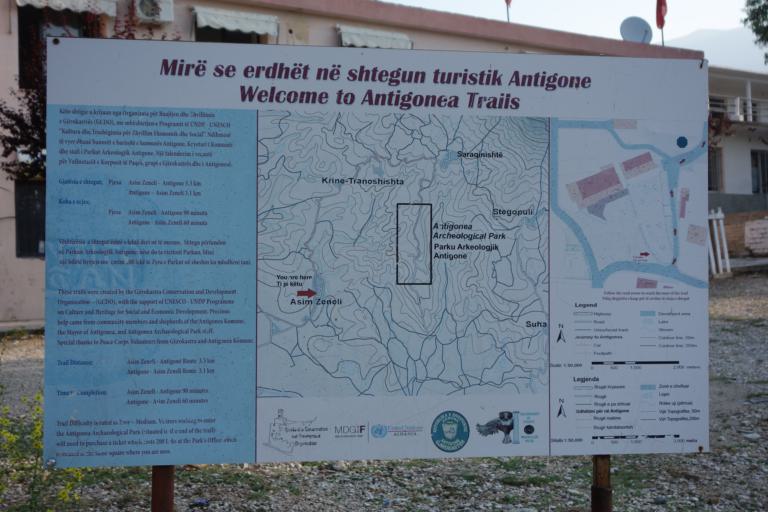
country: AL
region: Gjirokaster
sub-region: Rrethi i Gjirokastres
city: Qestorat
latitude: 40.0809
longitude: 20.1978
